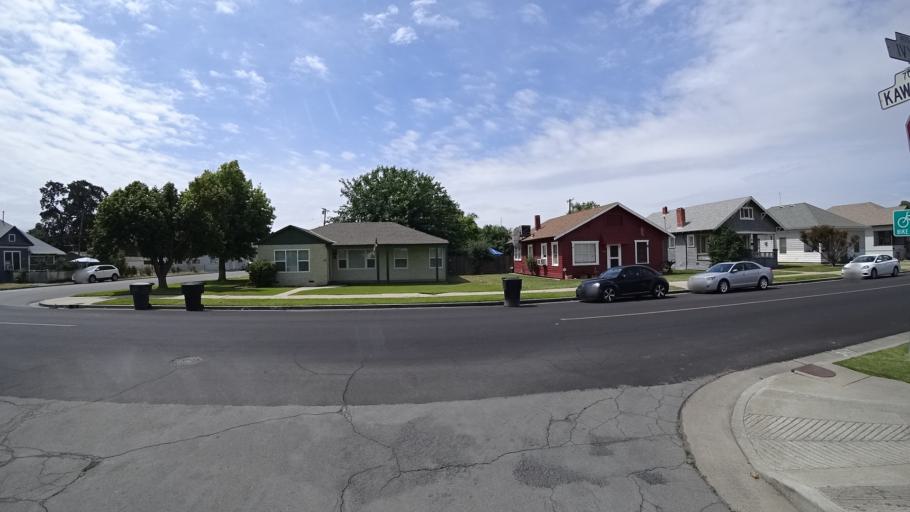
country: US
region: California
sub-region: Kings County
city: Hanford
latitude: 36.3323
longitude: -119.6510
